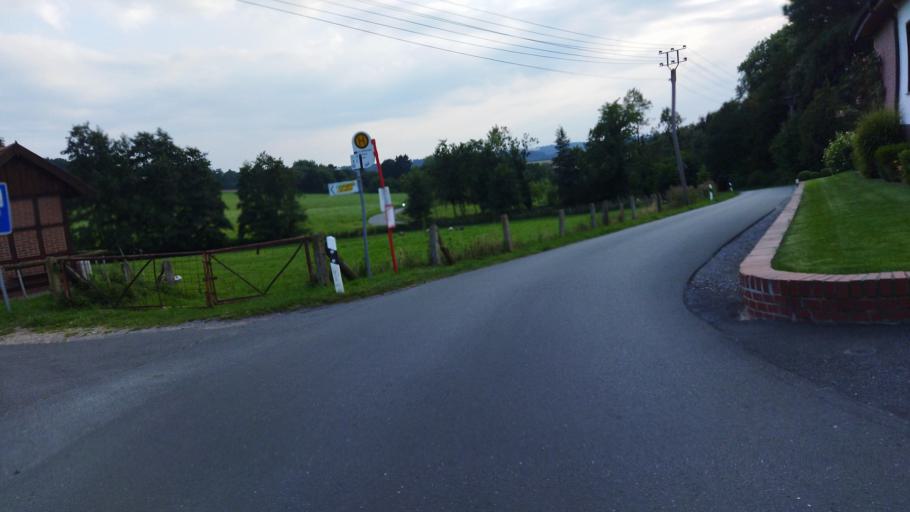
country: DE
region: Lower Saxony
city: Hagen
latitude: 52.1954
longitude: 8.0089
